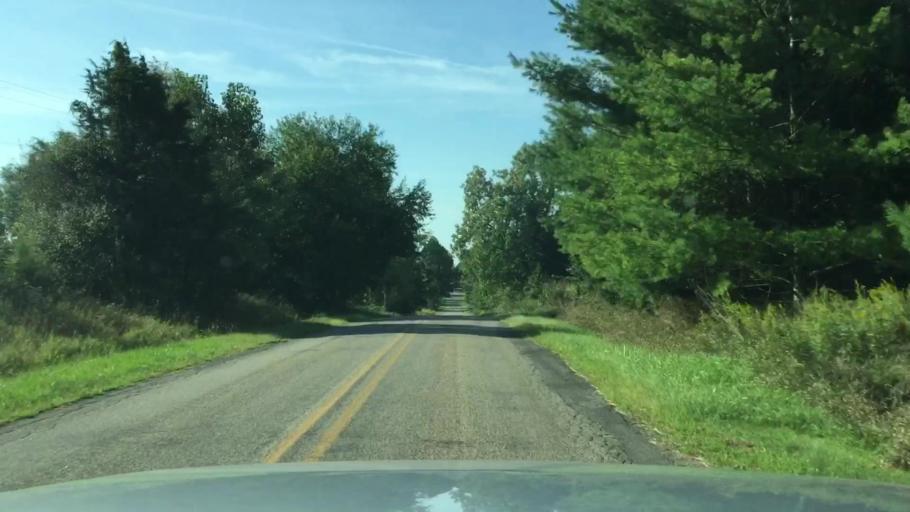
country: US
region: Michigan
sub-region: Lenawee County
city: Hudson
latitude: 41.8816
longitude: -84.4202
